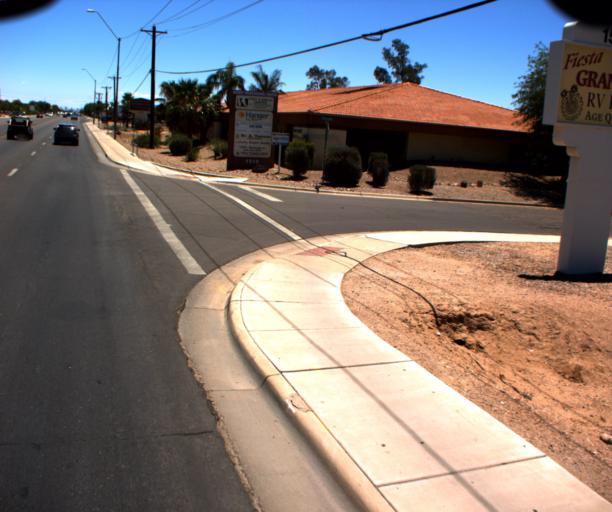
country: US
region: Arizona
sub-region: Pinal County
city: Casa Grande
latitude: 32.8795
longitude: -111.7209
